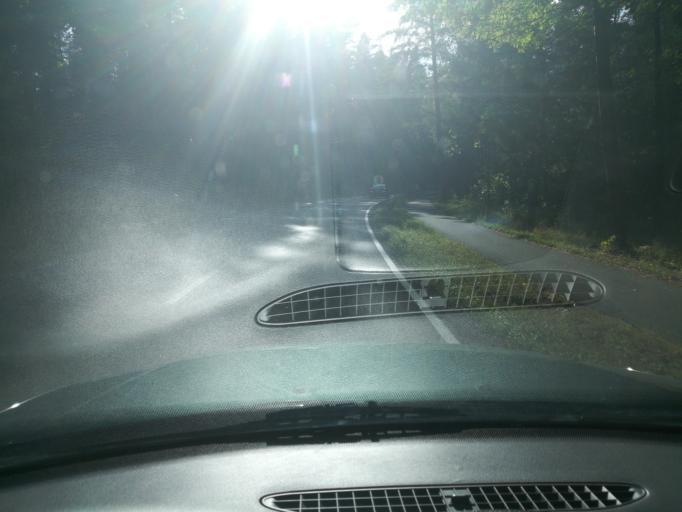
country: DE
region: Bavaria
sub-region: Regierungsbezirk Mittelfranken
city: Wetzendorf
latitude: 49.5285
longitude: 11.0725
